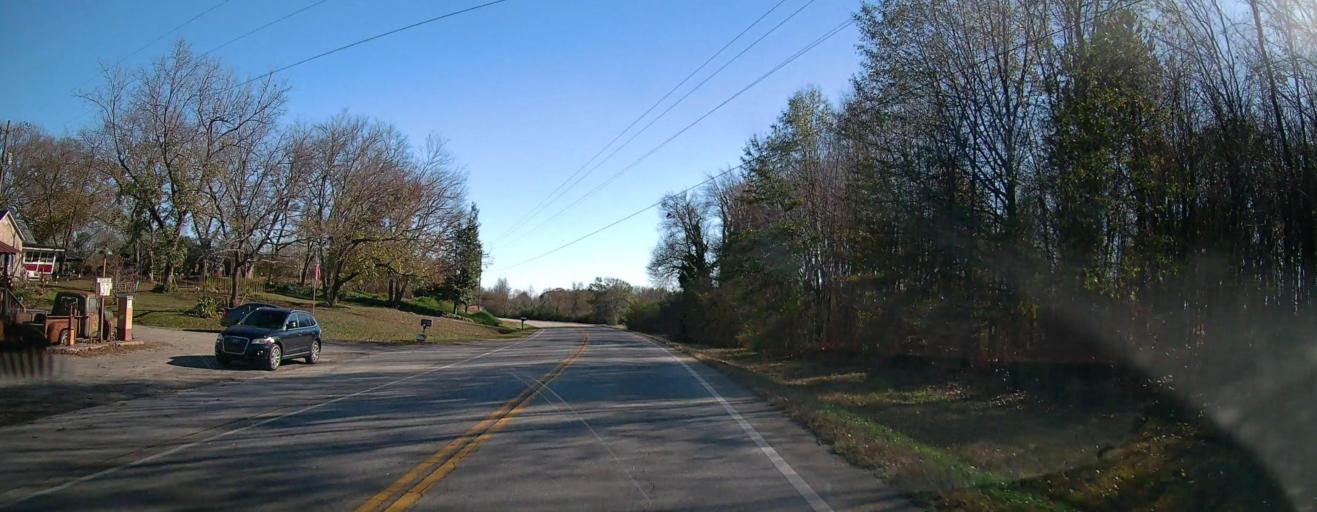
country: US
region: Georgia
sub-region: Hall County
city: Lula
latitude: 34.4604
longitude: -83.7336
